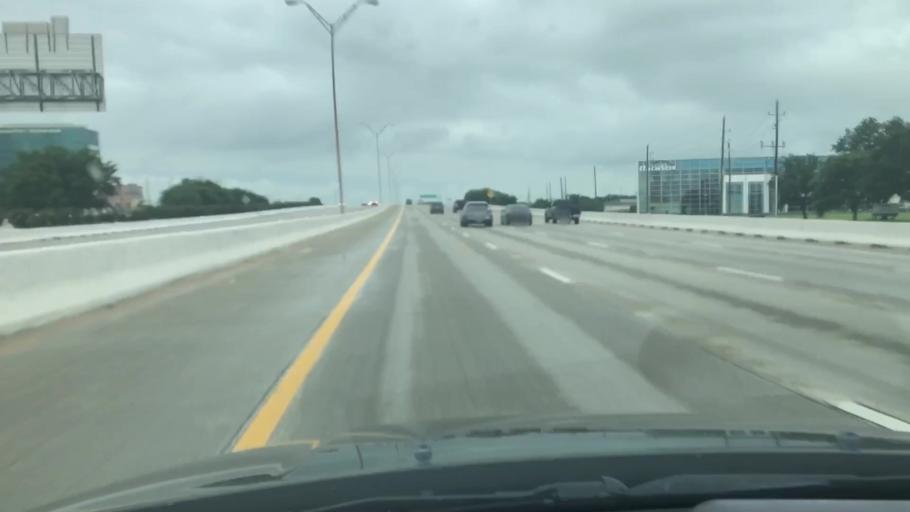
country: US
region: Texas
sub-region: Harris County
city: Bunker Hill Village
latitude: 29.7092
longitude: -95.5574
